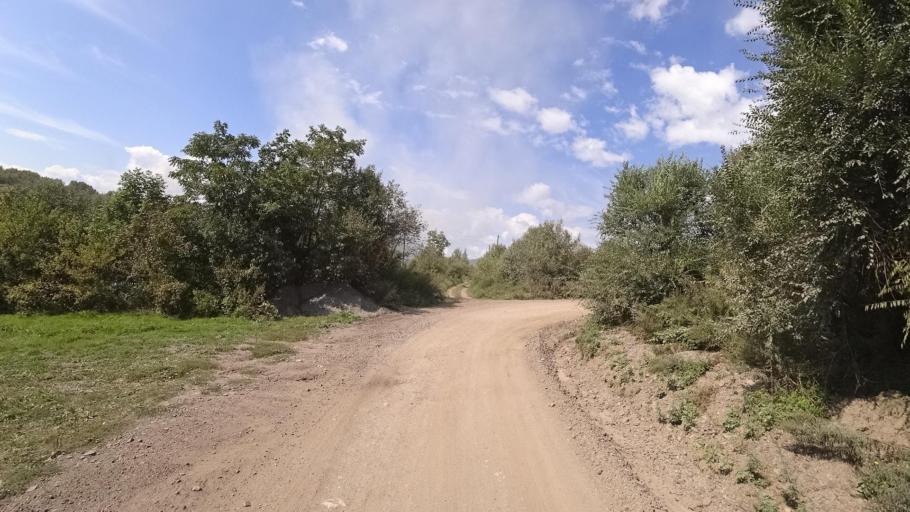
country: RU
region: Jewish Autonomous Oblast
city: Londoko
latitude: 49.0086
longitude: 131.9123
